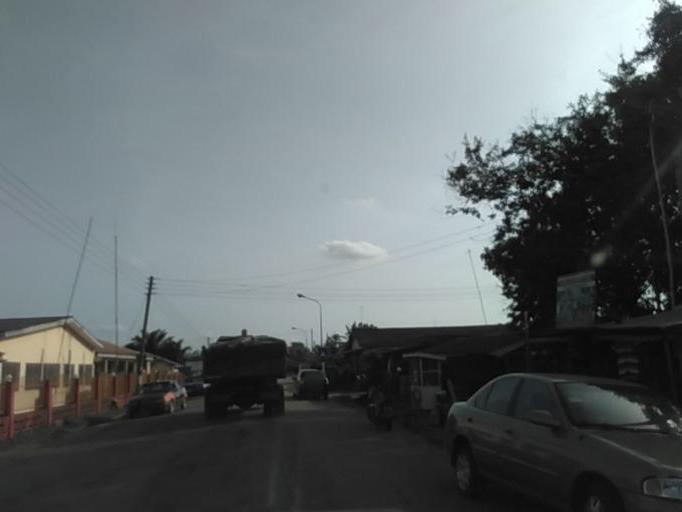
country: GH
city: Akropong
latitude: 6.0984
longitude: 0.1252
